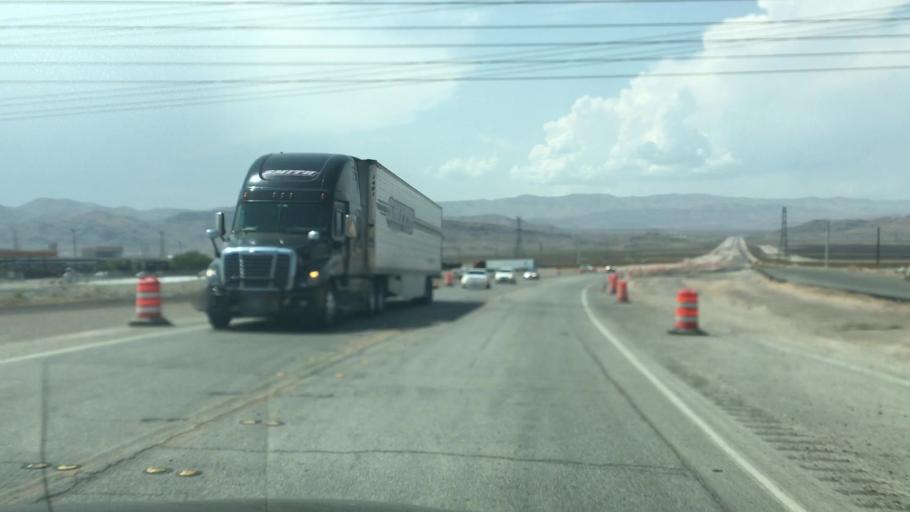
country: US
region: Nevada
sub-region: Clark County
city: Nellis Air Force Base
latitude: 36.3818
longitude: -114.8937
